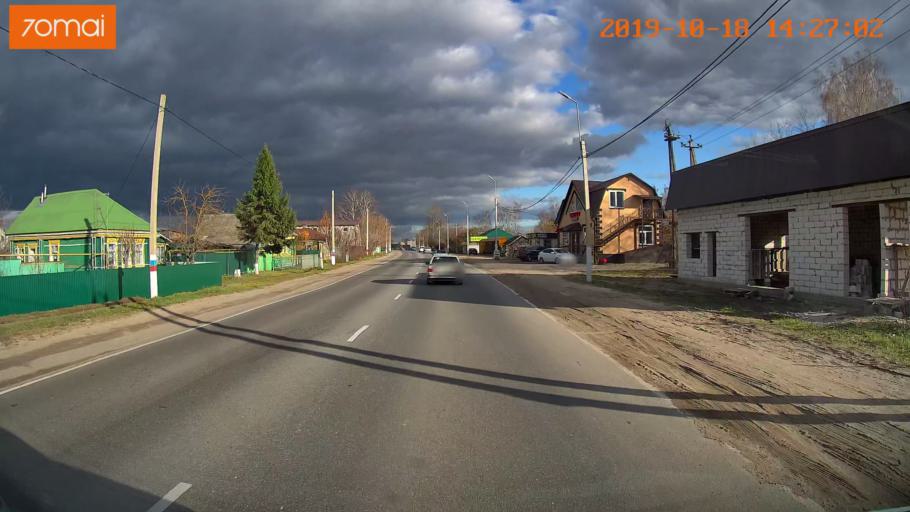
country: RU
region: Rjazan
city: Tuma
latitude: 55.1455
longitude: 40.5397
